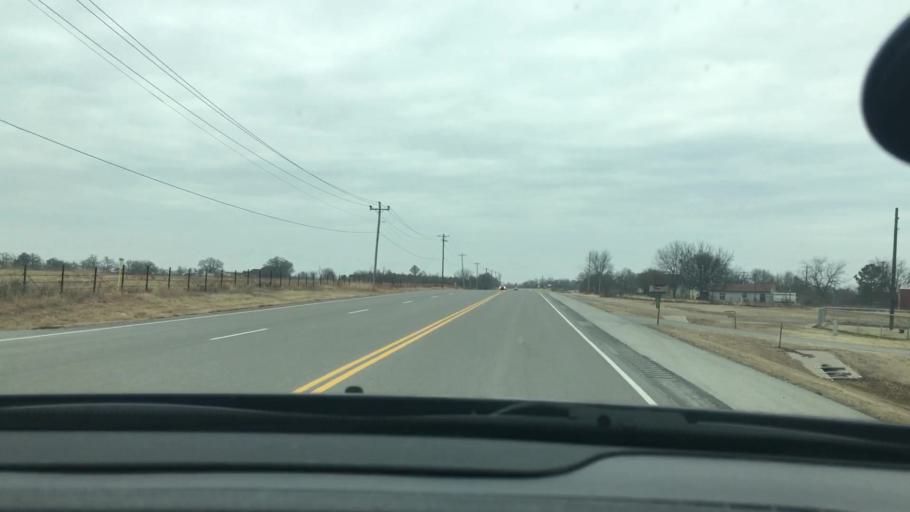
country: US
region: Oklahoma
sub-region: Carter County
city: Healdton
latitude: 34.3979
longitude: -97.5047
